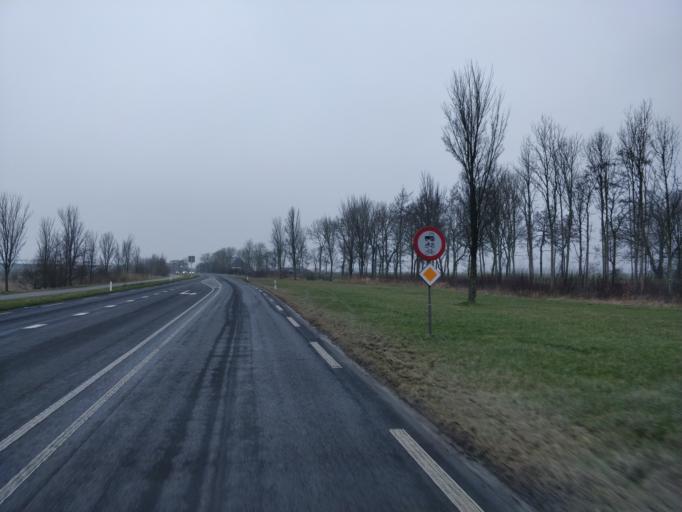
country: NL
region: Friesland
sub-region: Menameradiel
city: Menaam
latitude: 53.2383
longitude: 5.6782
